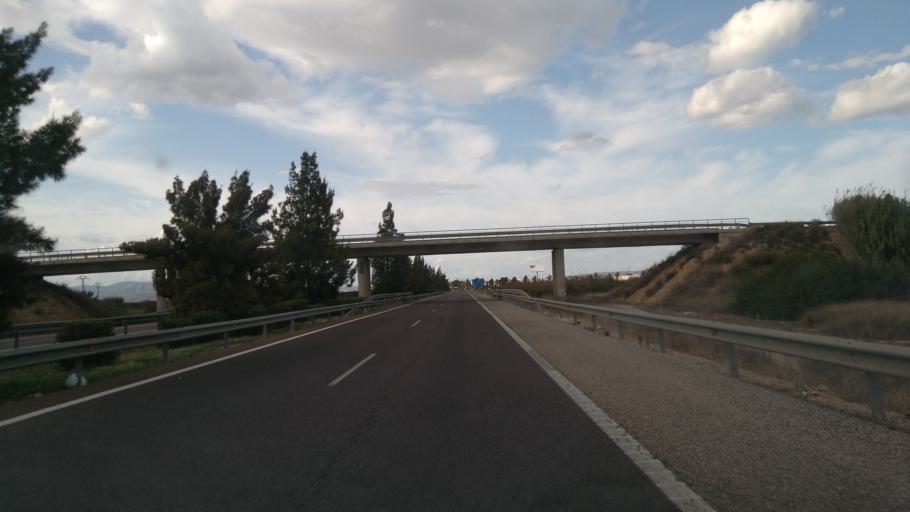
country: ES
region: Valencia
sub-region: Provincia de Valencia
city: Guadassuar
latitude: 39.1701
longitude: -0.4635
